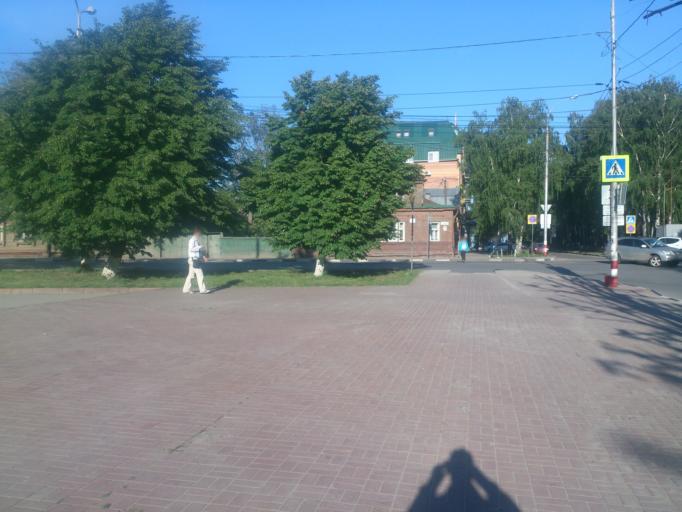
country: RU
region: Ulyanovsk
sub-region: Ulyanovskiy Rayon
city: Ulyanovsk
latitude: 54.3215
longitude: 48.4044
